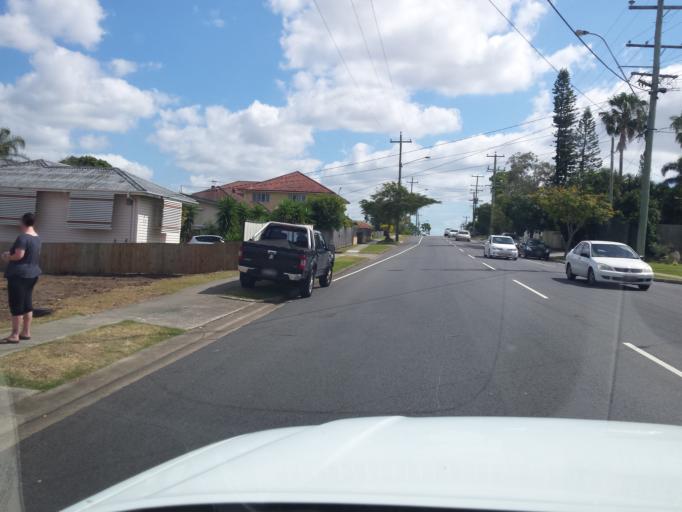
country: AU
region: Queensland
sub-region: Brisbane
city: Zillmere
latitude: -27.3733
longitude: 153.0356
